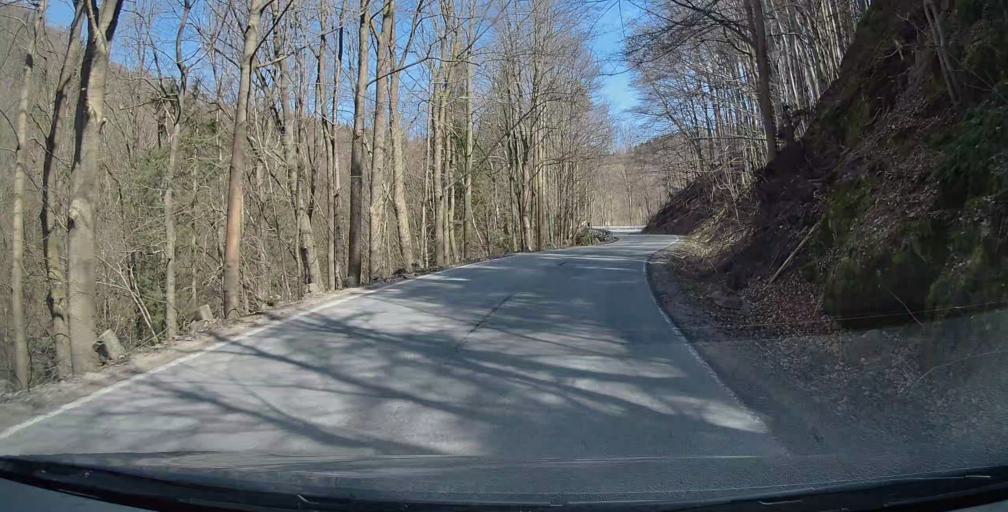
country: PL
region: Lower Silesian Voivodeship
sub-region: Powiat klodzki
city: Kudowa-Zdroj
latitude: 50.4501
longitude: 16.2780
